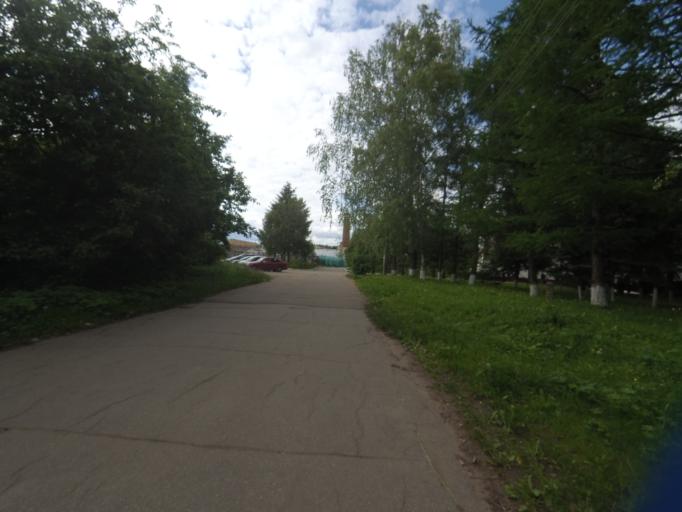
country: RU
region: Moskovskaya
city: Marfino
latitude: 56.0813
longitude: 37.5604
